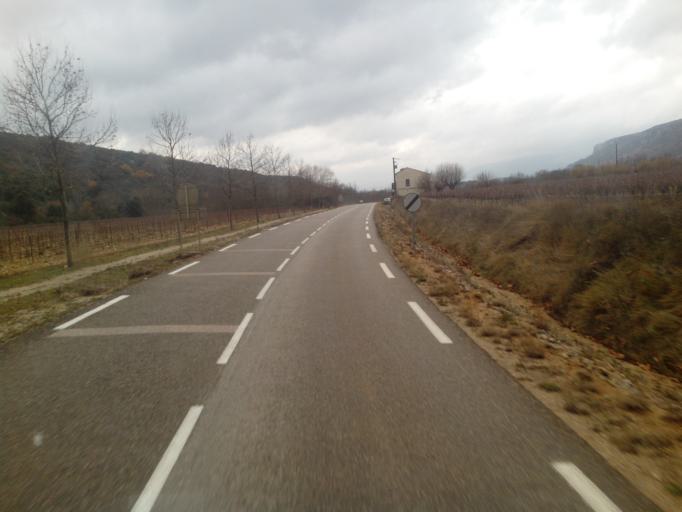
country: FR
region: Languedoc-Roussillon
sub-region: Departement de l'Herault
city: Saint-Bauzille-de-Putois
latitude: 43.9220
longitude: 3.7899
